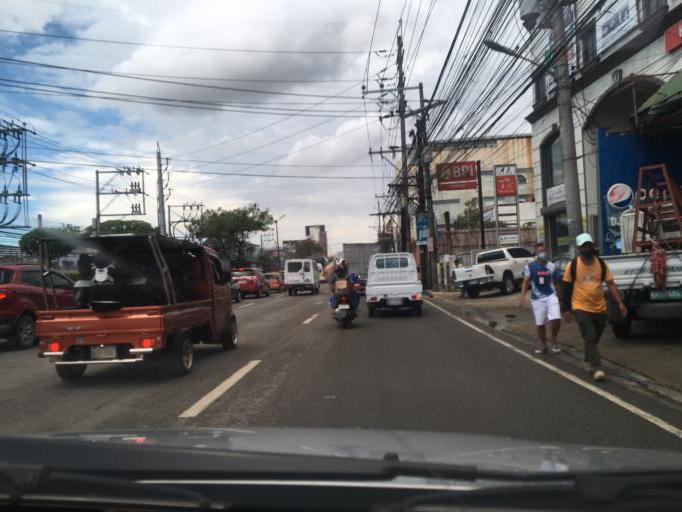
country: PH
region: Central Visayas
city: Mandaue City
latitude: 10.3338
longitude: 123.9376
